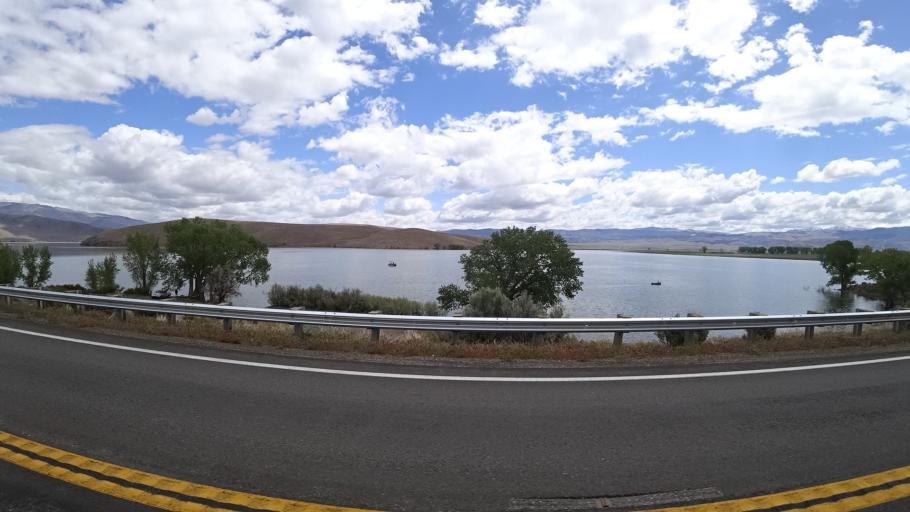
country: US
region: Nevada
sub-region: Lyon County
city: Smith Valley
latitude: 38.6610
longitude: -119.5400
